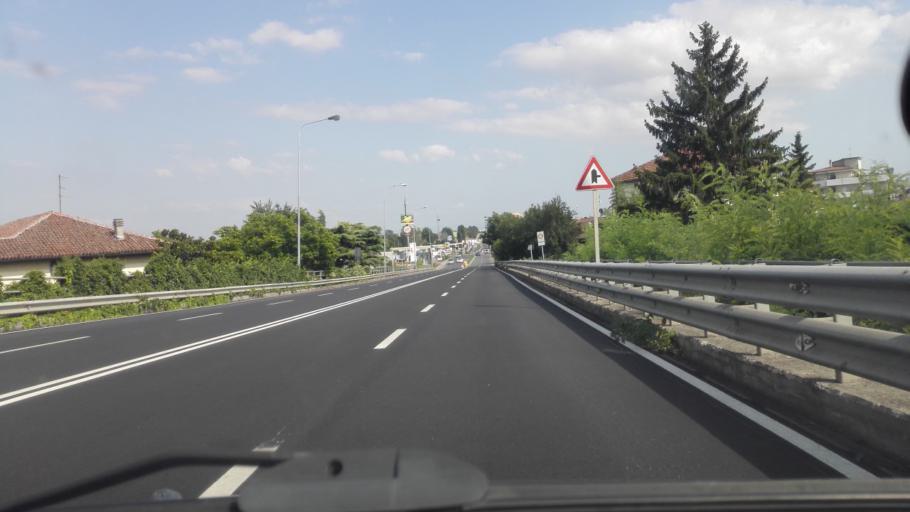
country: IT
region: Piedmont
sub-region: Provincia di Alessandria
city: Alessandria
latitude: 44.9220
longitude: 8.5896
